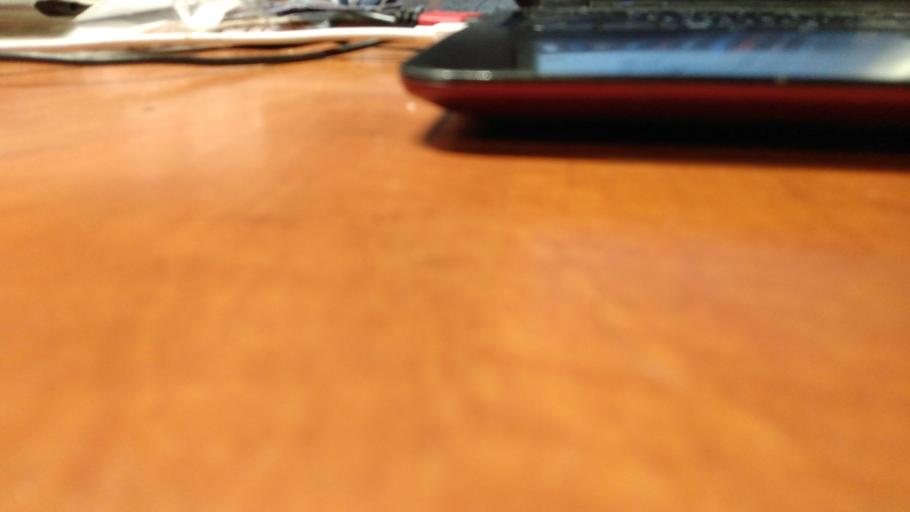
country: RU
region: Vologda
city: Babayevo
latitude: 59.1207
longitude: 36.1883
